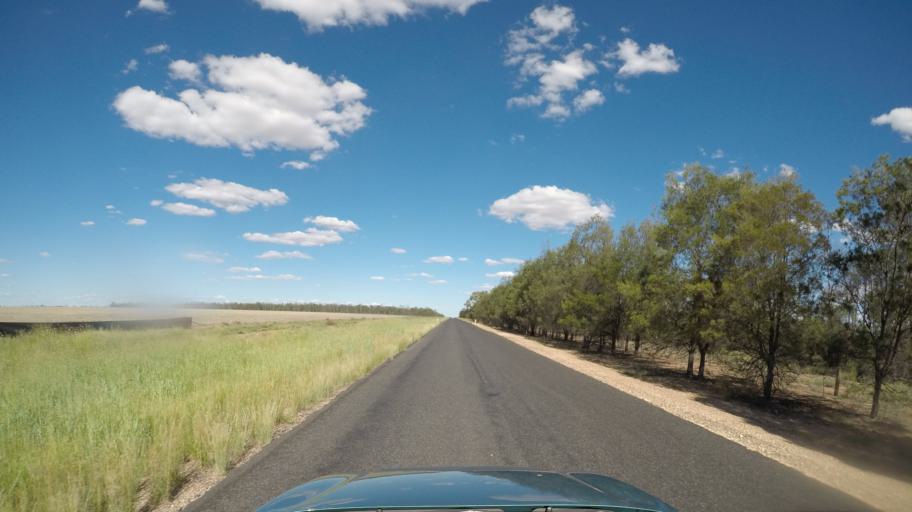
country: AU
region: Queensland
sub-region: Goondiwindi
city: Goondiwindi
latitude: -28.1718
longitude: 150.2253
